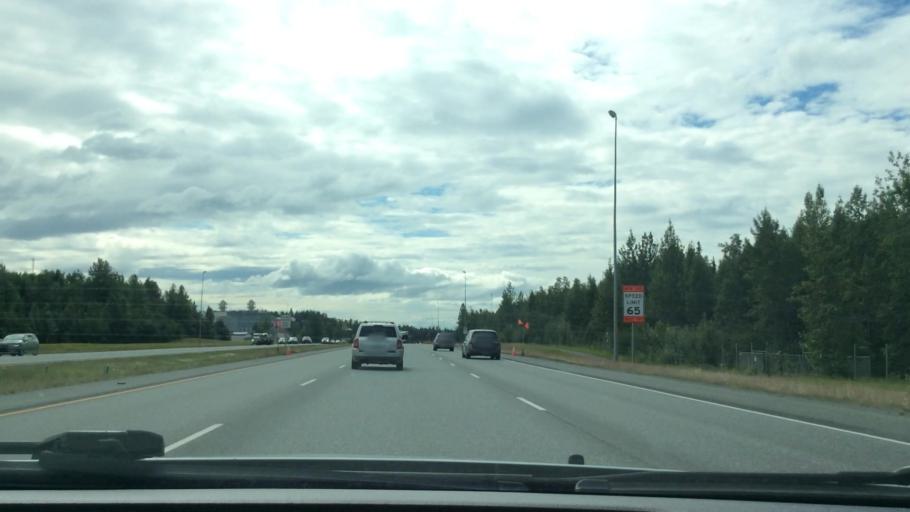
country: US
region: Alaska
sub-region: Anchorage Municipality
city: Elmendorf Air Force Base
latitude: 61.2345
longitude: -149.7051
